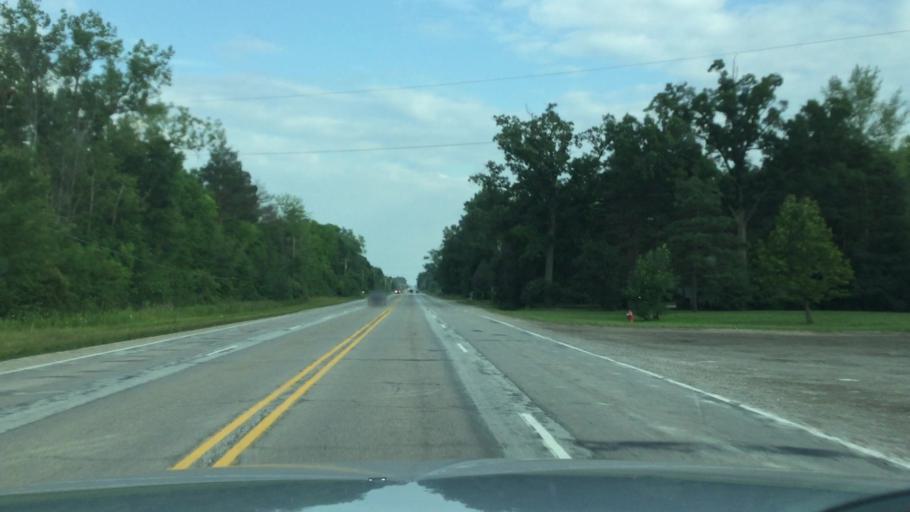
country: US
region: Michigan
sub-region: Saginaw County
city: Birch Run
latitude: 43.2786
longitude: -83.7908
